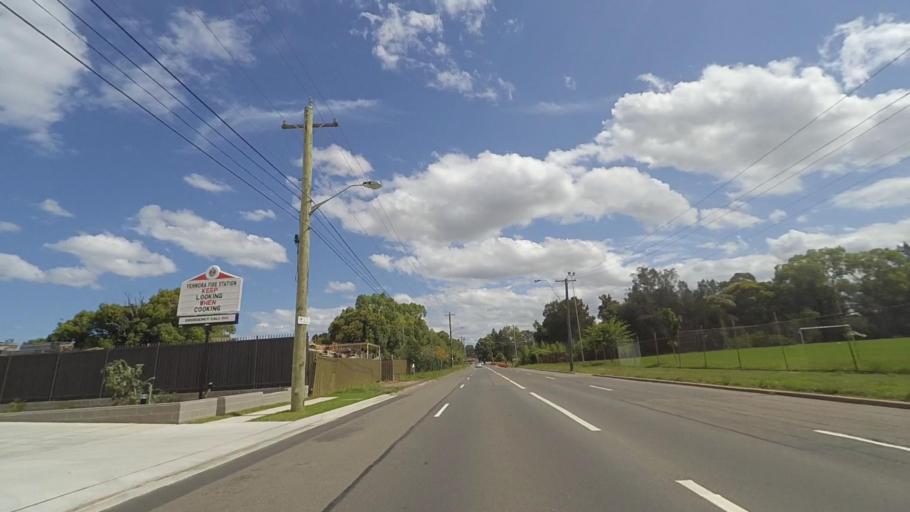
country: AU
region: New South Wales
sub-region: Fairfield
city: Fairfield East
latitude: -33.8588
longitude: 150.9583
